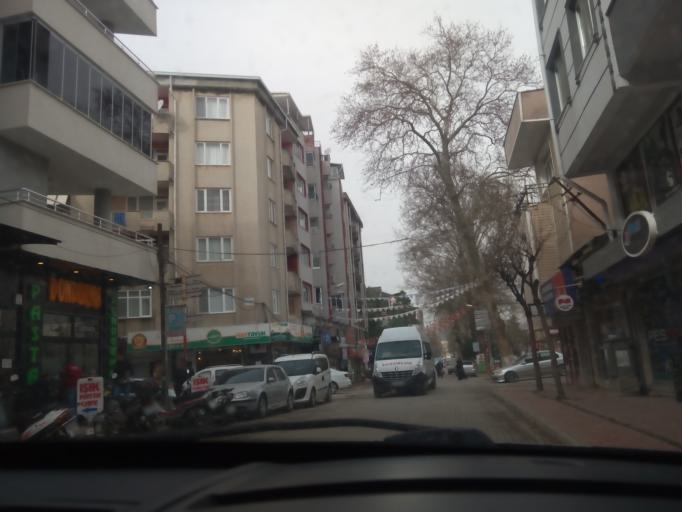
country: TR
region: Balikesir
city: Susurluk
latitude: 39.9163
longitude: 28.1563
